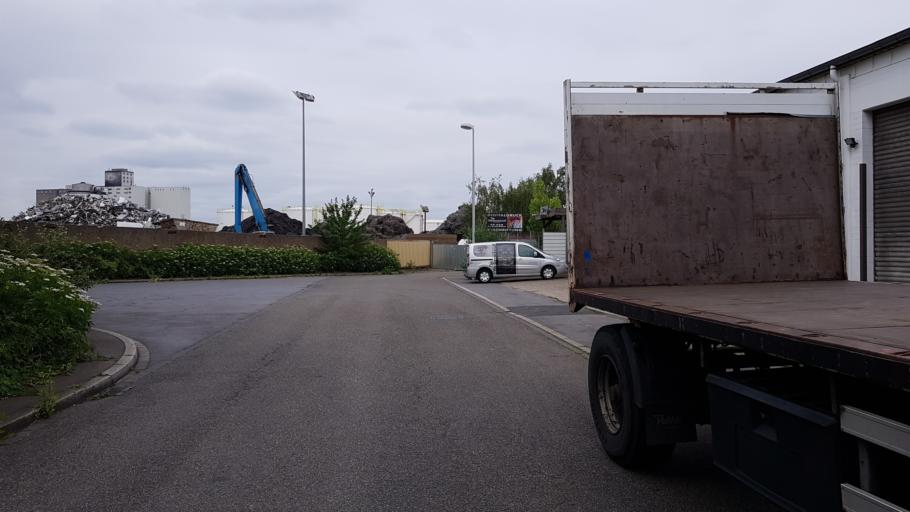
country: DE
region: North Rhine-Westphalia
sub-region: Regierungsbezirk Dusseldorf
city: Muelheim (Ruhr)
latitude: 51.4350
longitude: 6.8459
